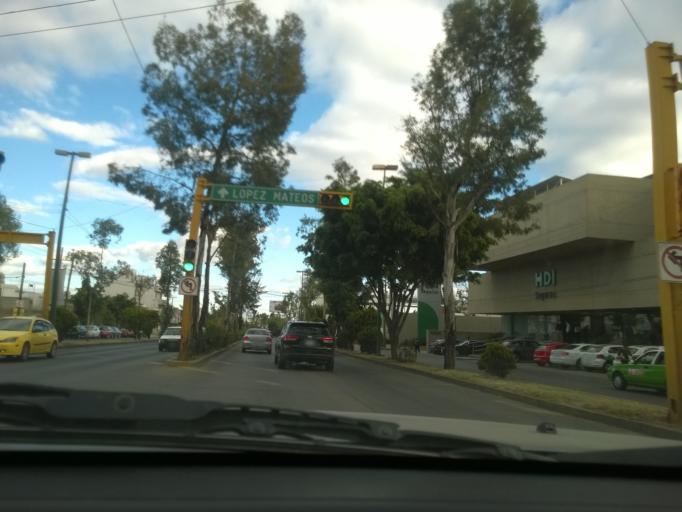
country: MX
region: Guanajuato
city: Leon
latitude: 21.1456
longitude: -101.6994
